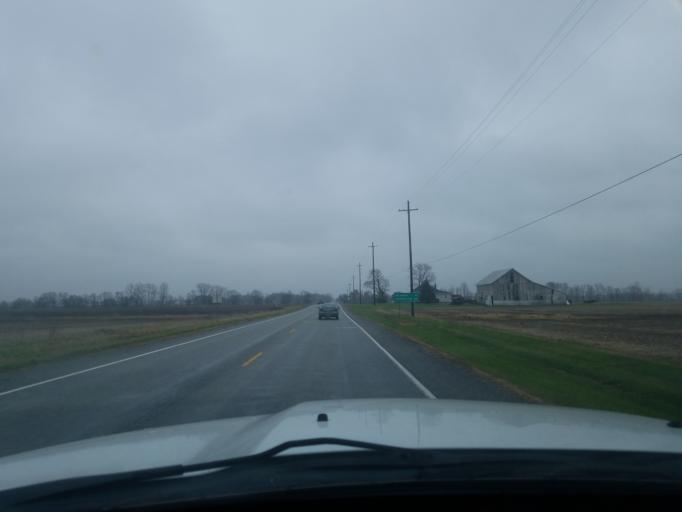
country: US
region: Indiana
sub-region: Howard County
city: Greentown
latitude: 40.4207
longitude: -85.9533
